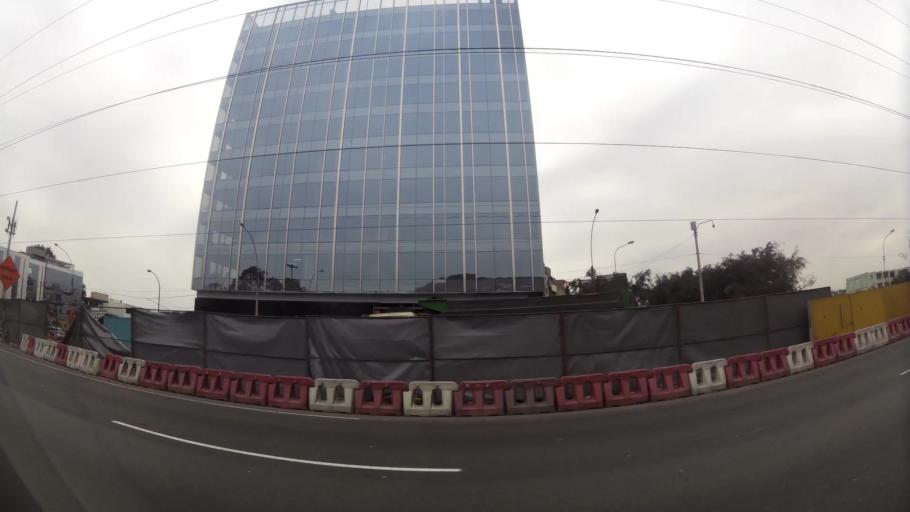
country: PE
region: Lima
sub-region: Lima
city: Surco
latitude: -12.1247
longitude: -76.9771
